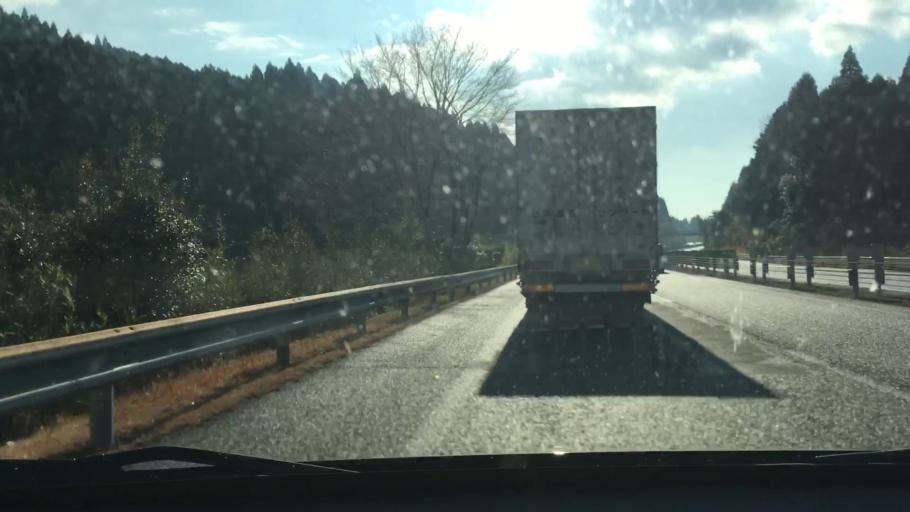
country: JP
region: Kagoshima
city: Okuchi-shinohara
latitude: 31.9600
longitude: 130.7427
